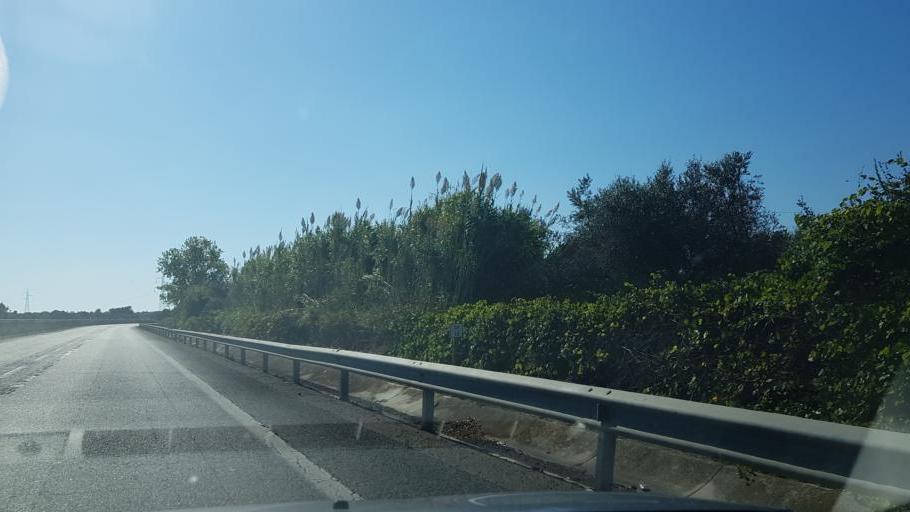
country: IT
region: Apulia
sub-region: Provincia di Brindisi
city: San Pietro Vernotico
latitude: 40.5152
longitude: 18.0212
